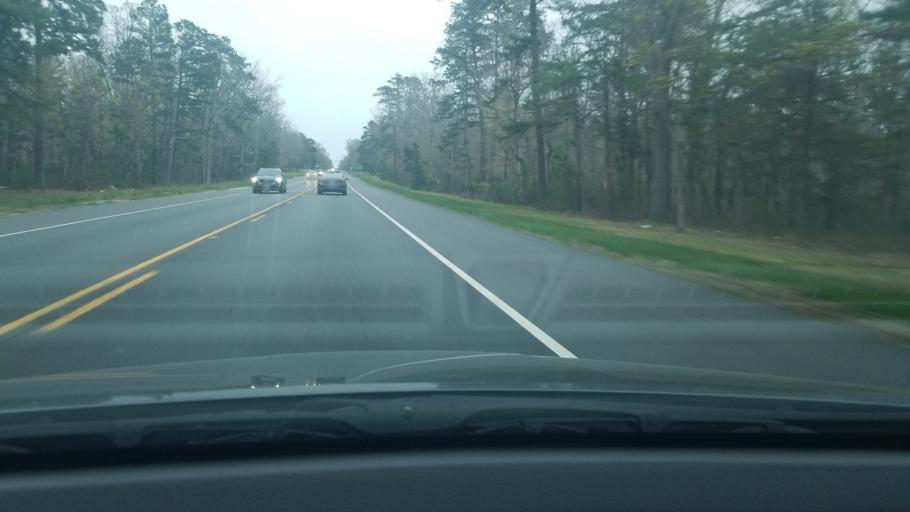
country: US
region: New Jersey
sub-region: Burlington County
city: Leisuretowne
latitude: 39.8880
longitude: -74.6618
